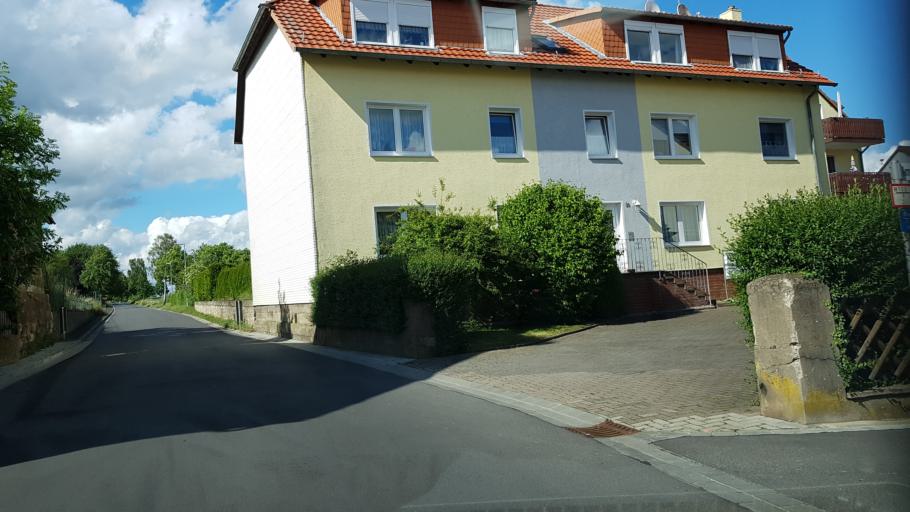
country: DE
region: Lower Saxony
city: Hardegsen
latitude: 51.6207
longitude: 9.8512
